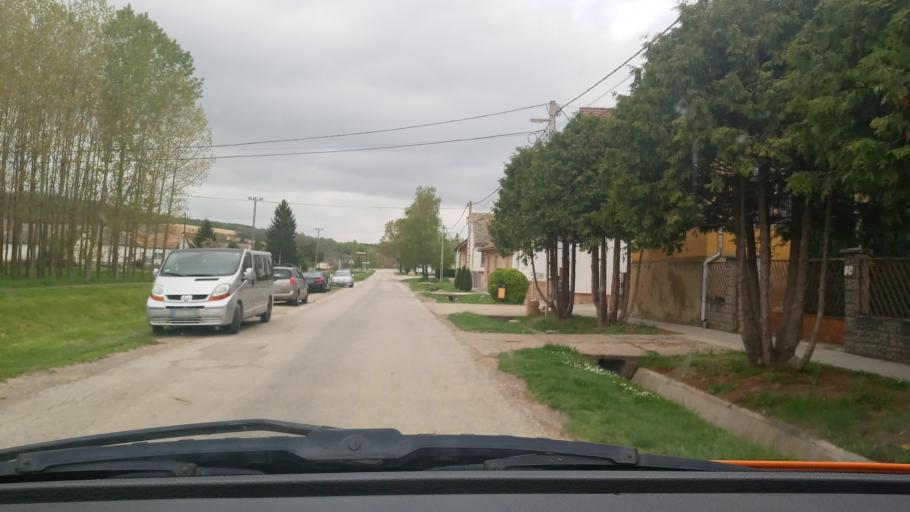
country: HU
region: Baranya
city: Boly
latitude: 46.0042
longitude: 18.5521
